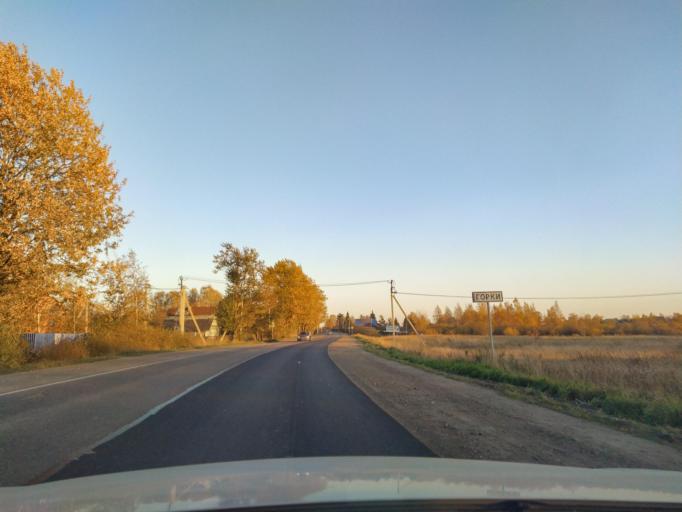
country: RU
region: Leningrad
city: Maloye Verevo
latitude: 59.6157
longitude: 30.2161
